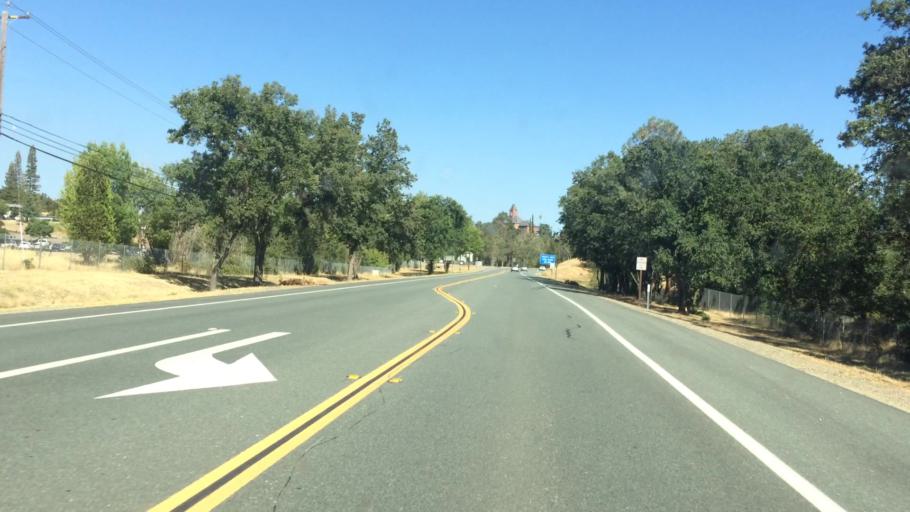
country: US
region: California
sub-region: Amador County
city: Ione
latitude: 38.3642
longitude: -120.9468
